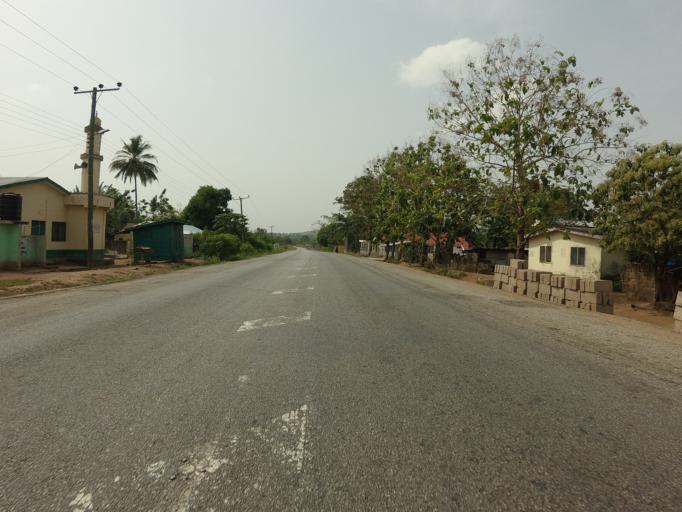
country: GH
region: Volta
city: Ho
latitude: 6.3305
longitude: 0.1655
